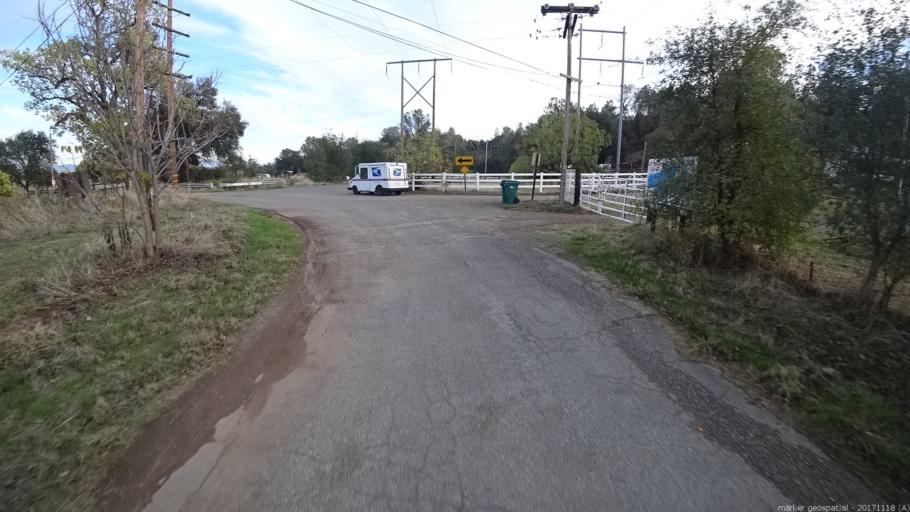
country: US
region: California
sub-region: Shasta County
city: Anderson
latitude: 40.4569
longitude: -122.3392
